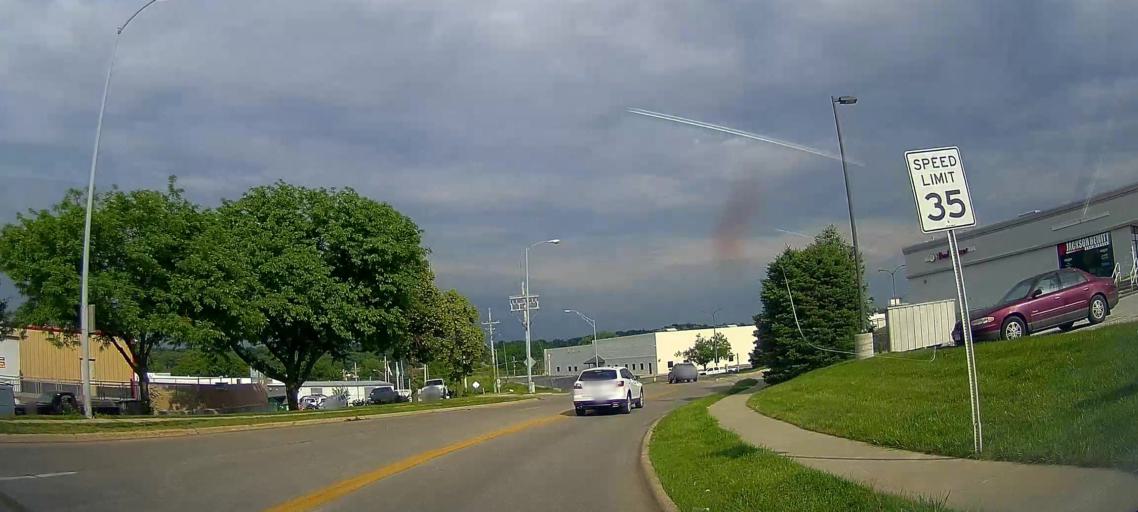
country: US
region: Nebraska
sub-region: Douglas County
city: Ralston
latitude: 41.3108
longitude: -96.0521
